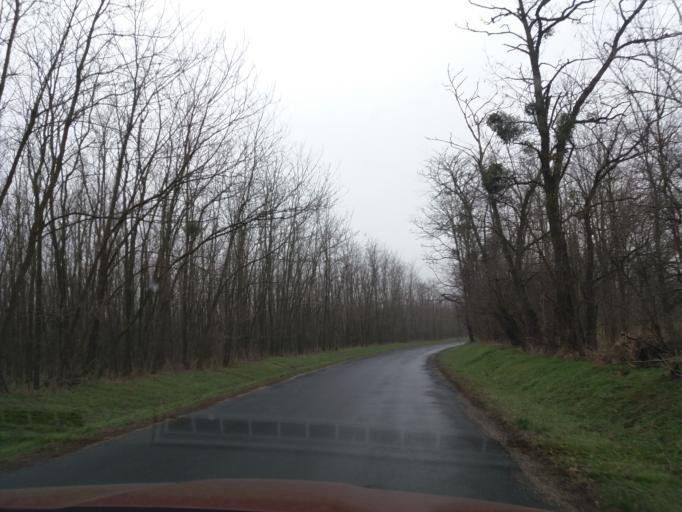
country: HU
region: Vas
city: Janoshaza
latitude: 47.0966
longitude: 17.2458
